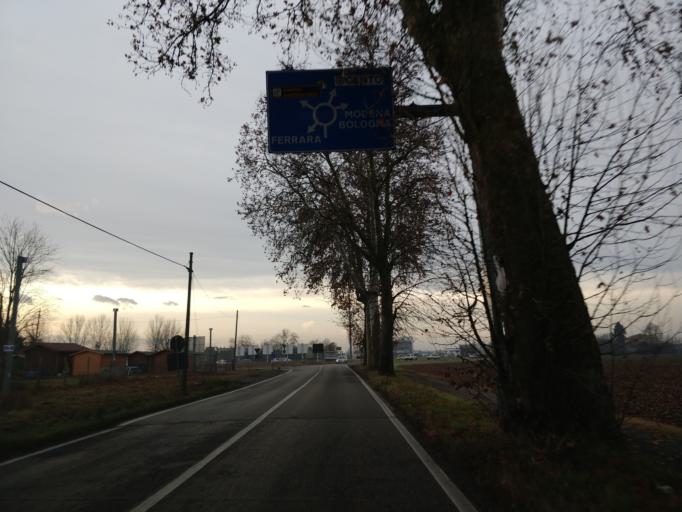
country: IT
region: Emilia-Romagna
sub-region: Provincia di Ferrara
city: Corpo Reno
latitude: 44.7510
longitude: 11.3000
